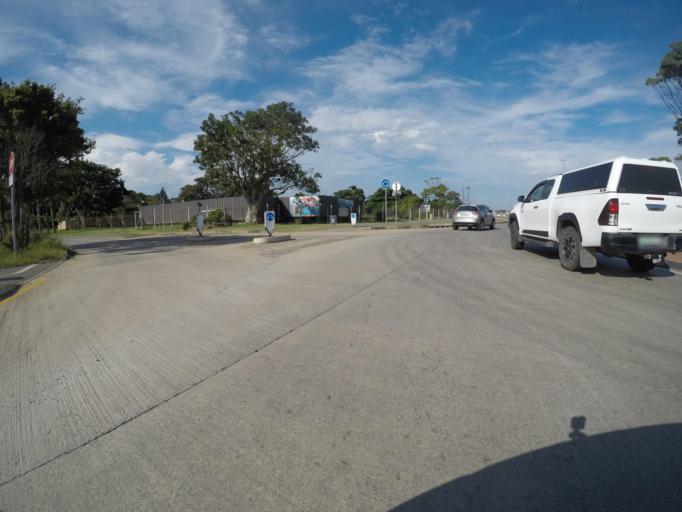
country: ZA
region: Eastern Cape
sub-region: Buffalo City Metropolitan Municipality
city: East London
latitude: -32.9373
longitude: 27.9826
